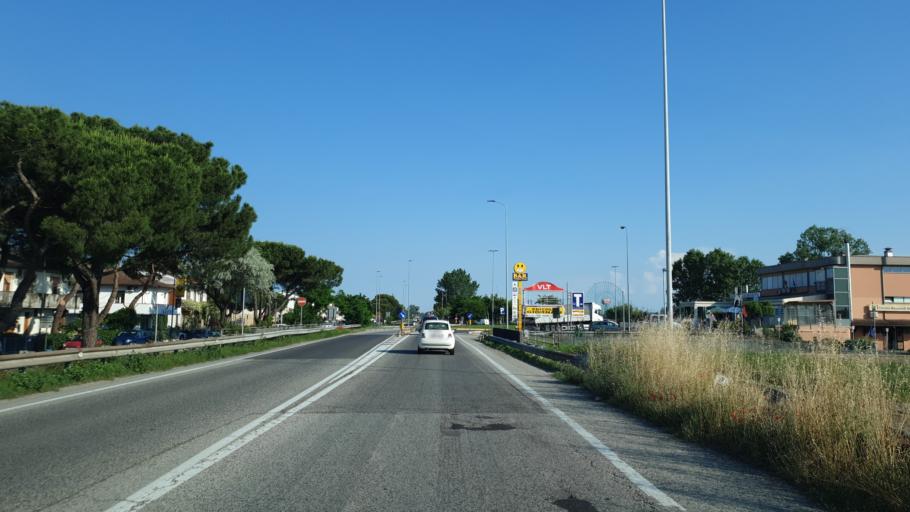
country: IT
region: Emilia-Romagna
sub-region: Provincia di Ravenna
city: Fosso Ghiaia
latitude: 44.3526
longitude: 12.2575
